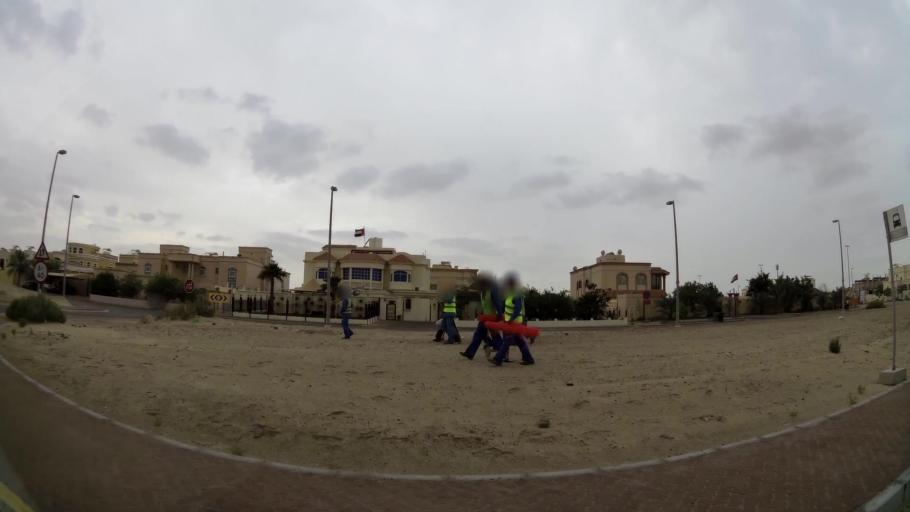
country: AE
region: Abu Dhabi
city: Abu Dhabi
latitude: 24.3757
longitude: 54.6454
